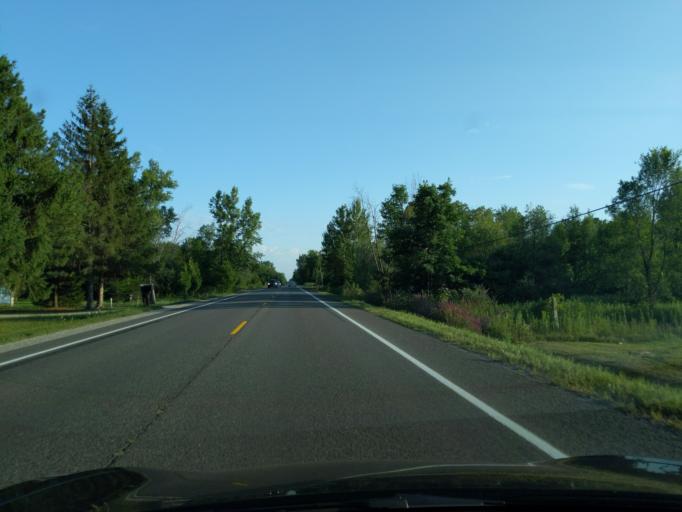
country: US
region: Michigan
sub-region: Midland County
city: Midland
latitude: 43.5797
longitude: -84.3695
